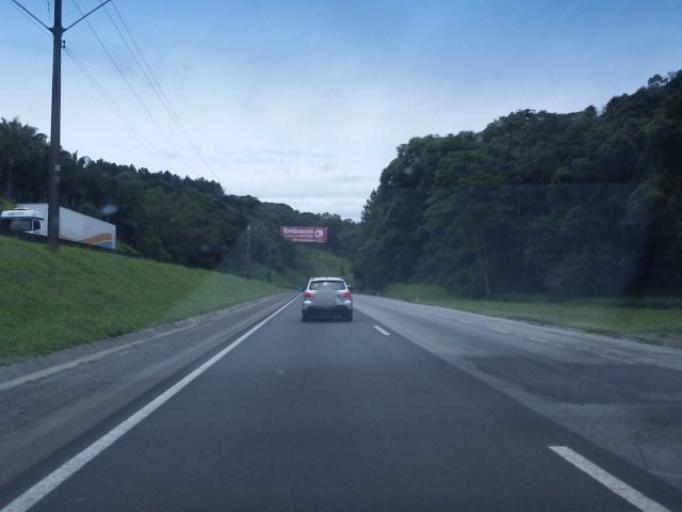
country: BR
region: Sao Paulo
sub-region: Juquitiba
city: Juquitiba
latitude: -23.9275
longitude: -46.9951
